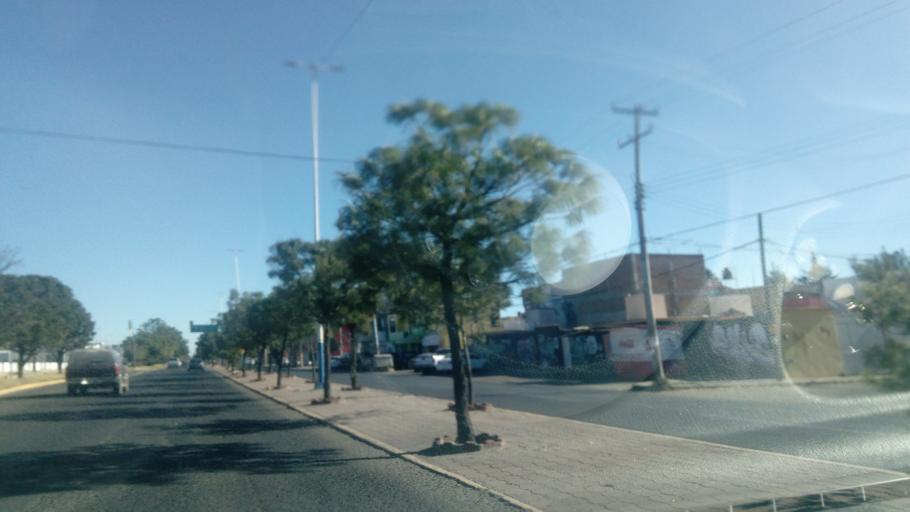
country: MX
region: Durango
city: Victoria de Durango
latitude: 24.0493
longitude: -104.6209
